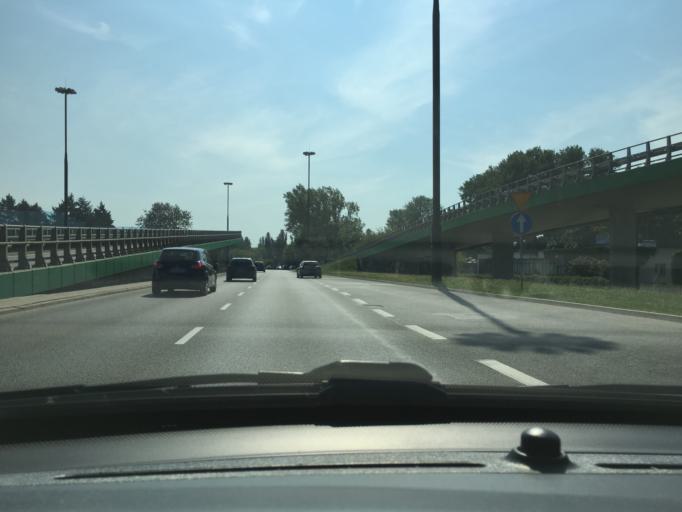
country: PL
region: Masovian Voivodeship
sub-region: Warszawa
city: Praga Polnoc
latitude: 52.2263
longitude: 21.0544
